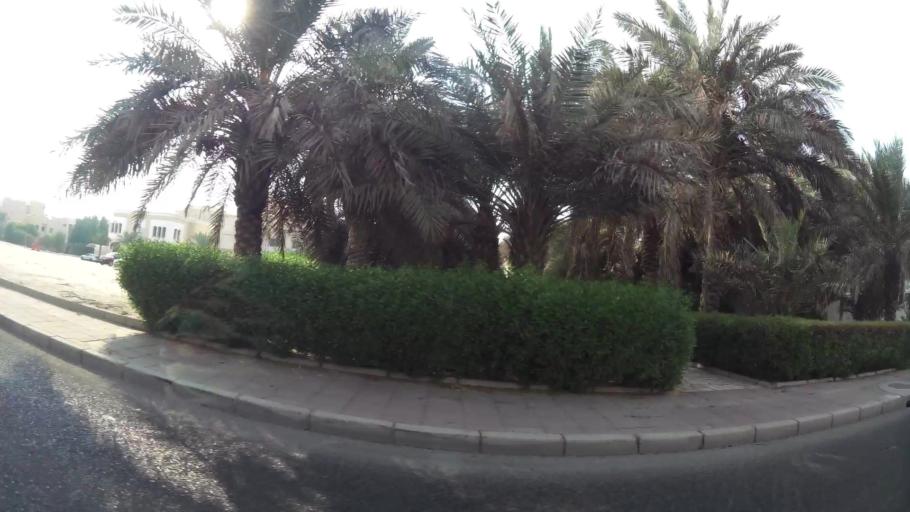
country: KW
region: Al Farwaniyah
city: Janub as Surrah
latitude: 29.3076
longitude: 47.9890
